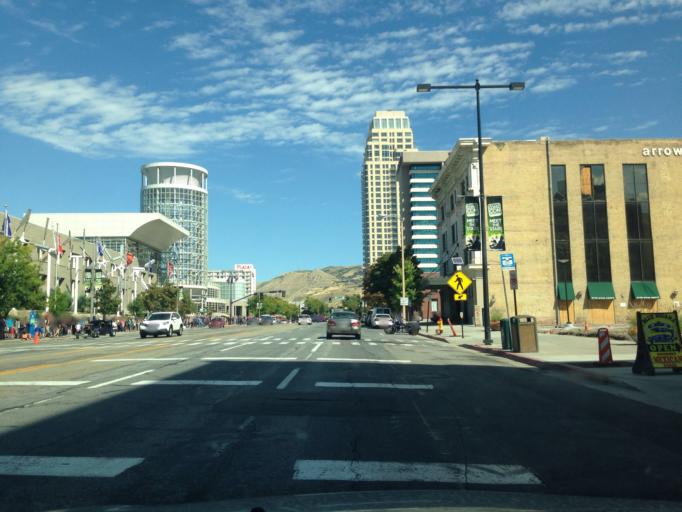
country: US
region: Utah
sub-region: Salt Lake County
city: Salt Lake City
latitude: 40.7658
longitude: -111.8939
